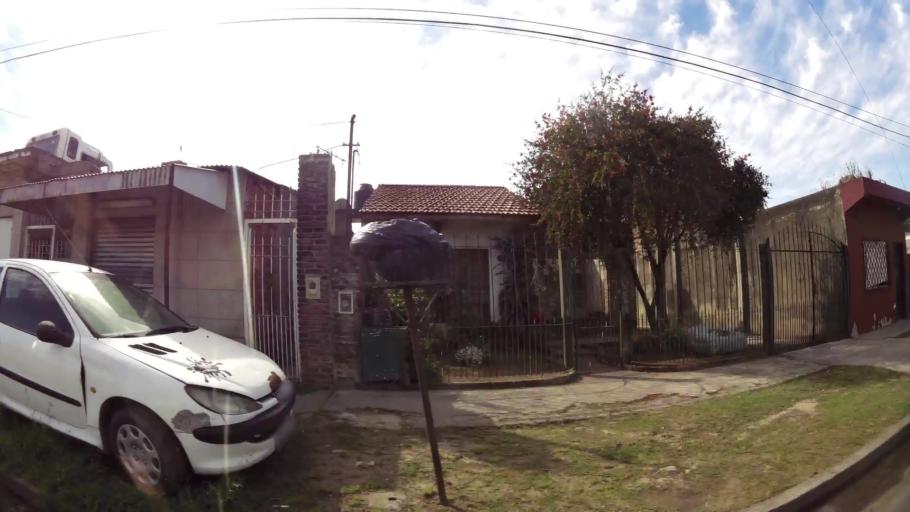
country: AR
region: Buenos Aires
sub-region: Partido de Quilmes
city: Quilmes
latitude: -34.7841
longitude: -58.3019
